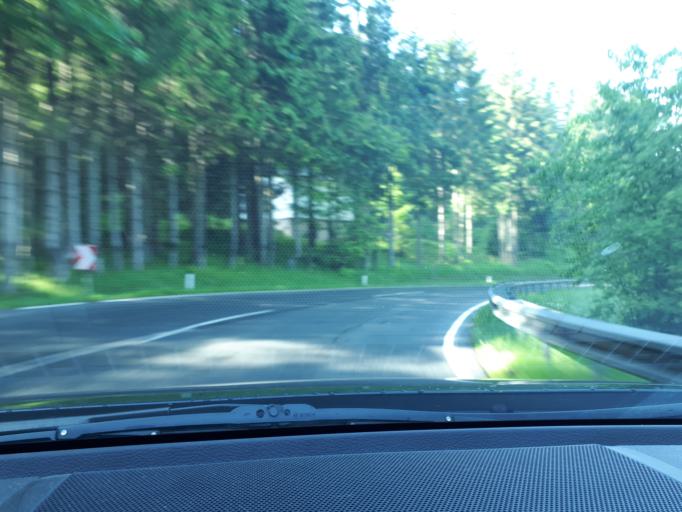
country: AT
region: Styria
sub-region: Politischer Bezirk Voitsberg
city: Pack
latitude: 46.9455
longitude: 14.9689
